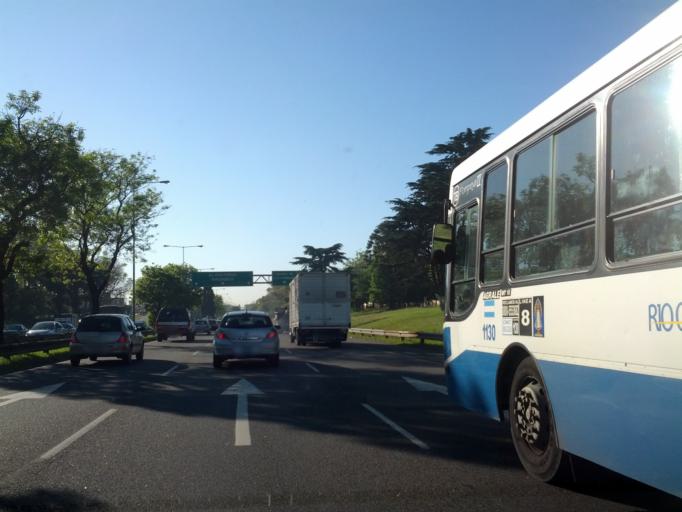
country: AR
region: Buenos Aires F.D.
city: Villa Lugano
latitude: -34.6670
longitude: -58.5117
